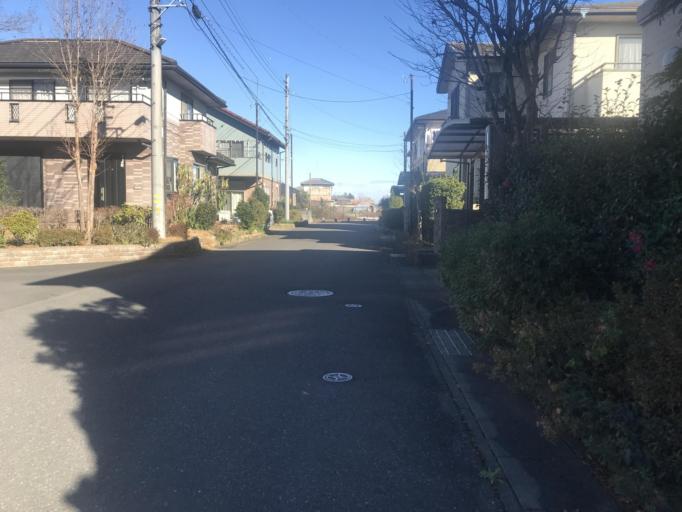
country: JP
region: Ibaraki
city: Yuki
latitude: 36.3115
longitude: 139.8771
